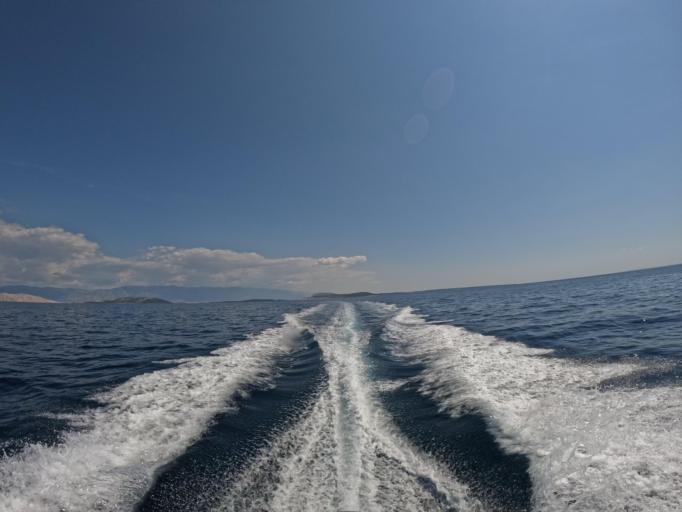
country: HR
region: Primorsko-Goranska
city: Lopar
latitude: 44.8866
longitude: 14.6405
